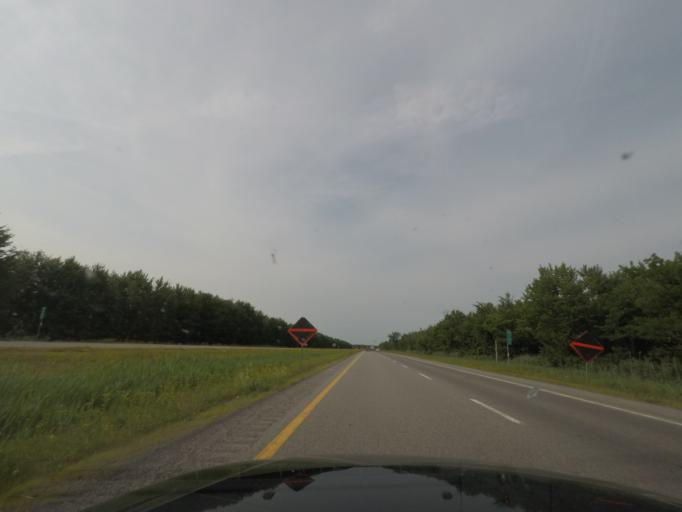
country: CA
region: Quebec
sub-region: Monteregie
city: Napierville
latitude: 45.1514
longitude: -73.4677
